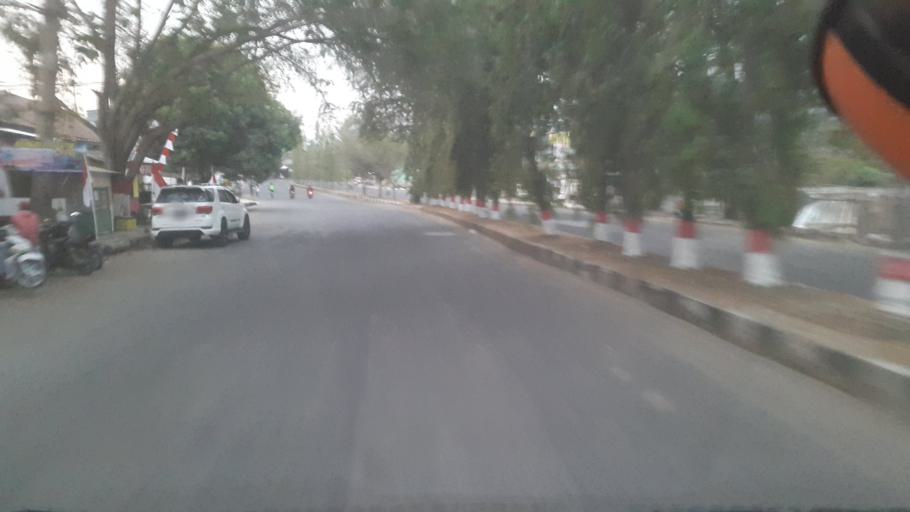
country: ID
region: West Java
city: Pelabuhanratu
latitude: -6.9926
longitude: 106.5574
